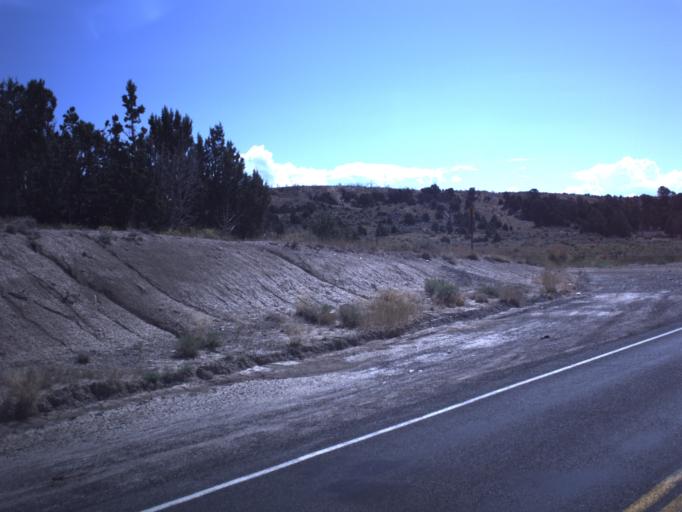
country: US
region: Utah
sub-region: Utah County
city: Genola
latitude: 39.9566
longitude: -112.2426
